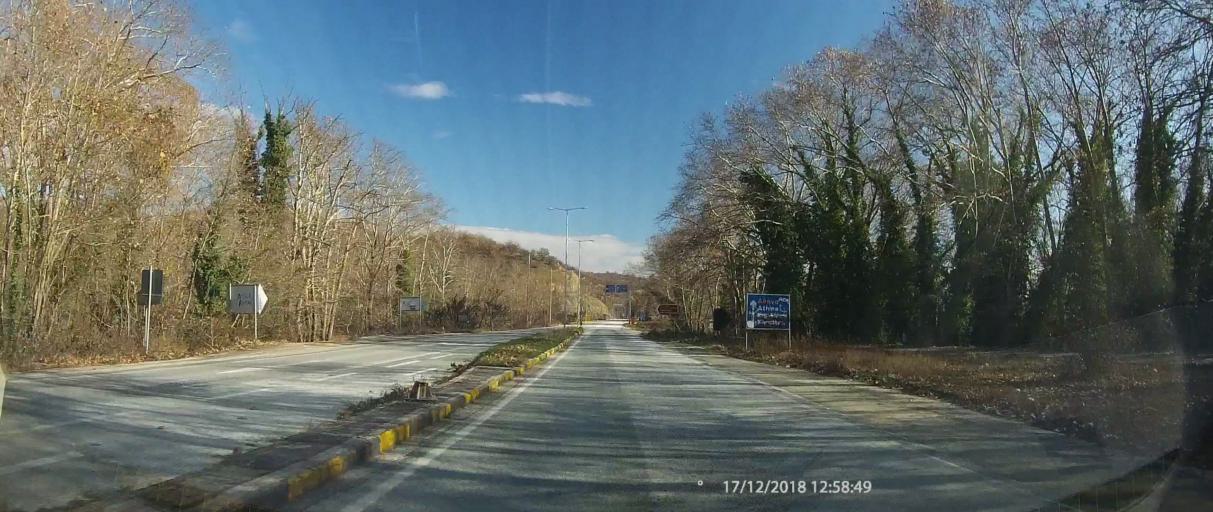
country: GR
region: Thessaly
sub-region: Trikala
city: Kastraki
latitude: 39.7387
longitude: 21.5477
